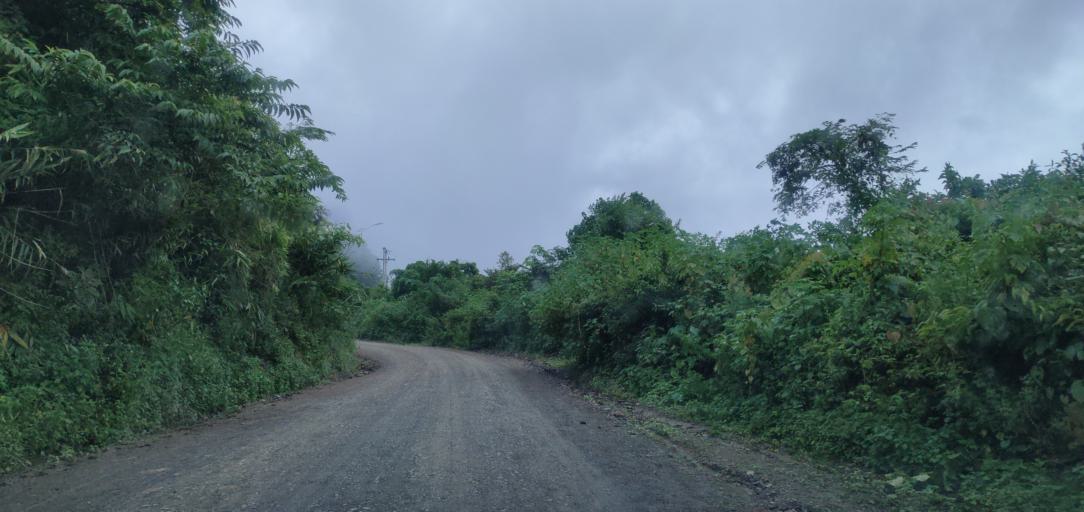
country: LA
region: Phongsali
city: Phongsali
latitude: 21.4516
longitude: 102.1623
